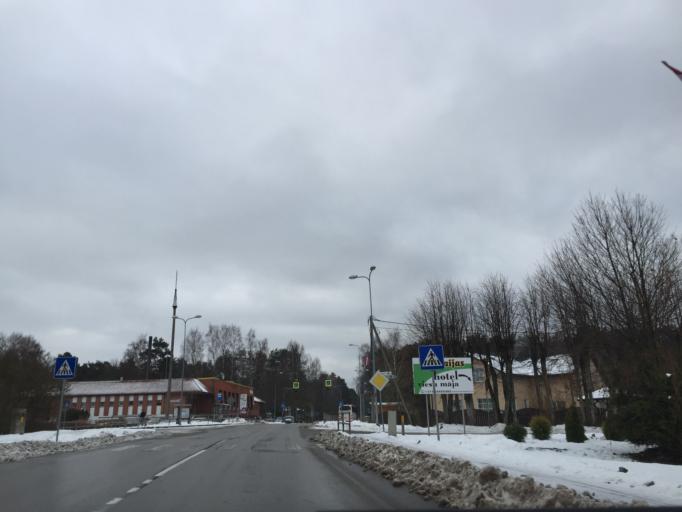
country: LV
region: Saulkrastu
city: Saulkrasti
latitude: 57.2567
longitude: 24.4151
